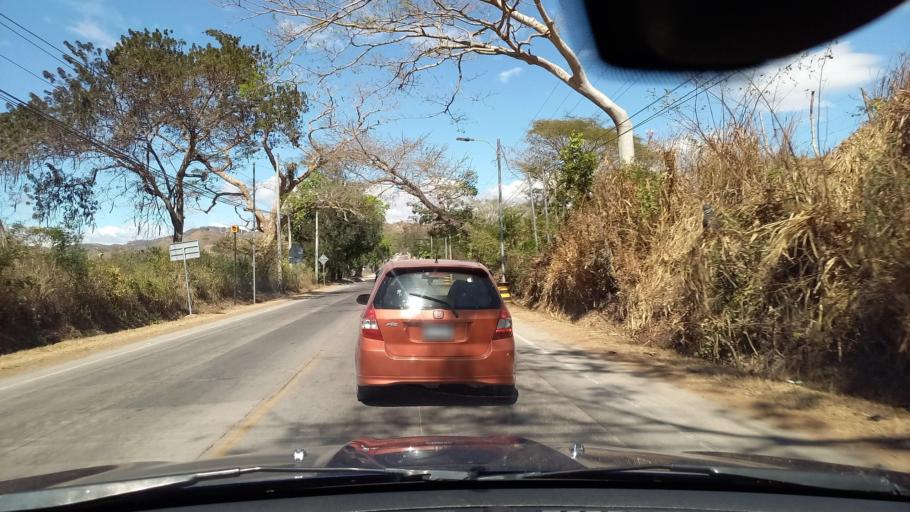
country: SV
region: Santa Ana
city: Metapan
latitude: 14.3389
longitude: -89.4494
